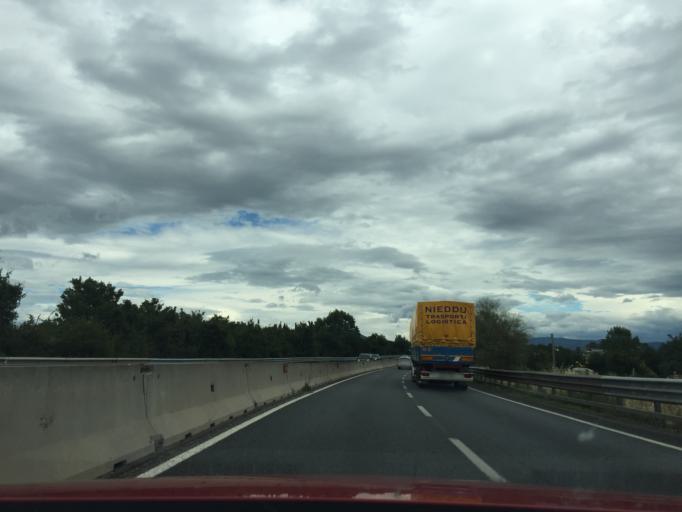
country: IT
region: Tuscany
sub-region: Province of Florence
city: Lastra a Signa
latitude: 43.7721
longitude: 11.1286
